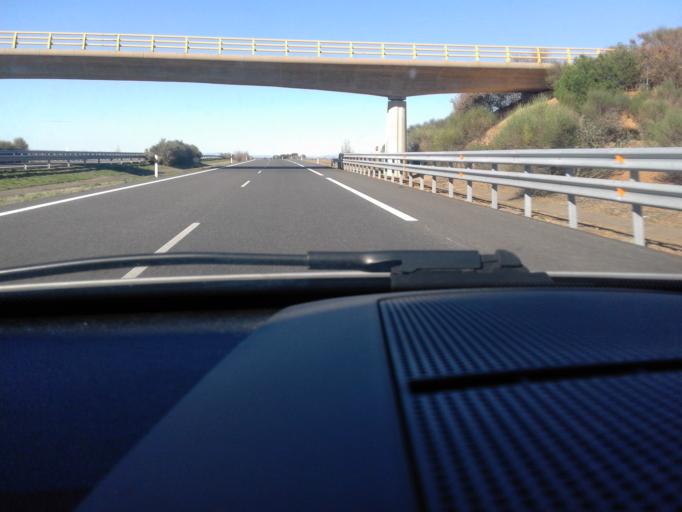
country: ES
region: Castille and Leon
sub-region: Provincia de Leon
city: Villamoratiel de las Matas
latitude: 42.4282
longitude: -5.2975
